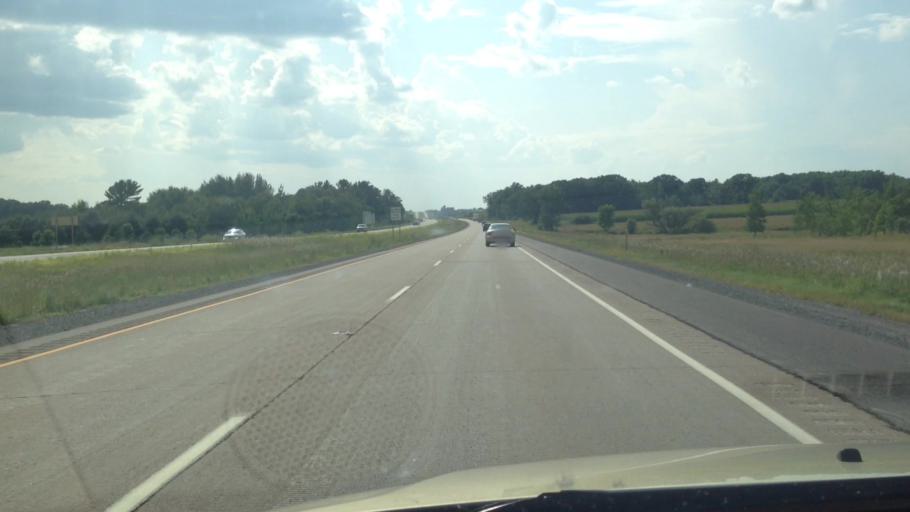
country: US
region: Wisconsin
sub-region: Clark County
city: Thorp
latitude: 44.9521
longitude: -90.8216
